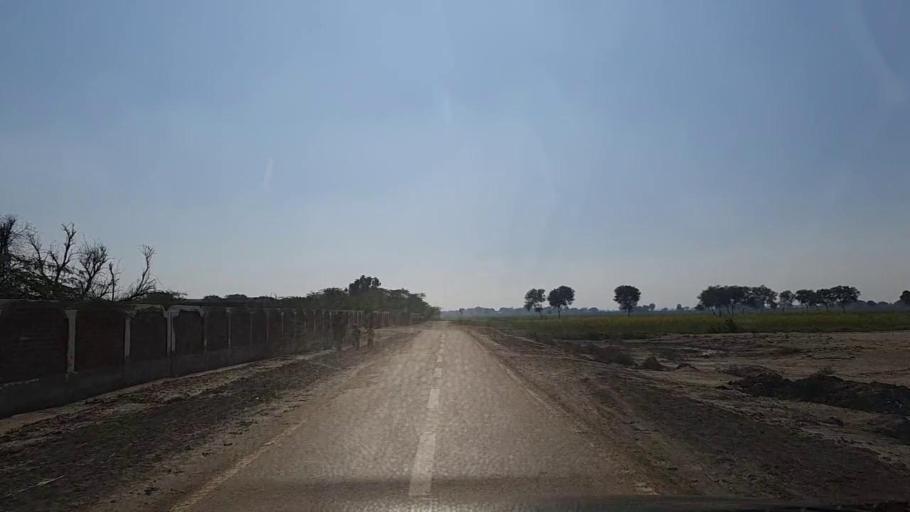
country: PK
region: Sindh
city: Nawabshah
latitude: 26.3196
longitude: 68.3449
